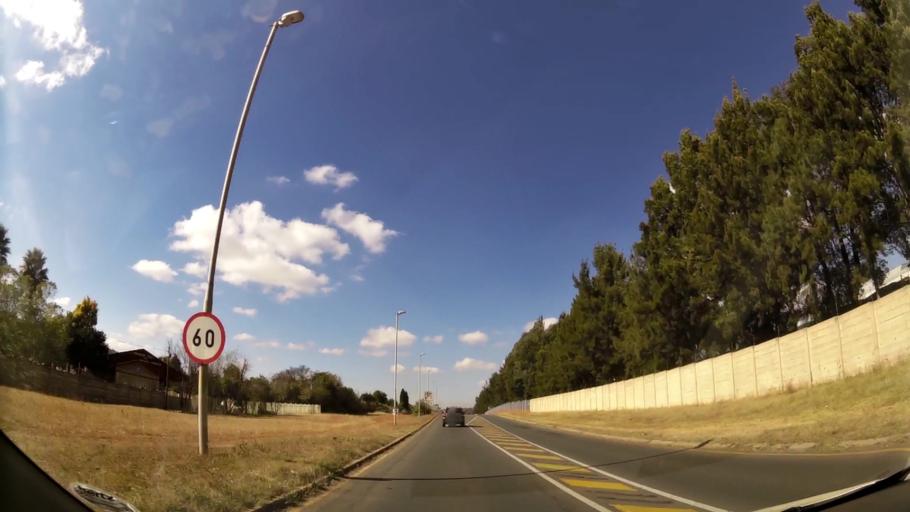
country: ZA
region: Gauteng
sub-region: West Rand District Municipality
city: Krugersdorp
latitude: -26.0999
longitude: 27.8342
